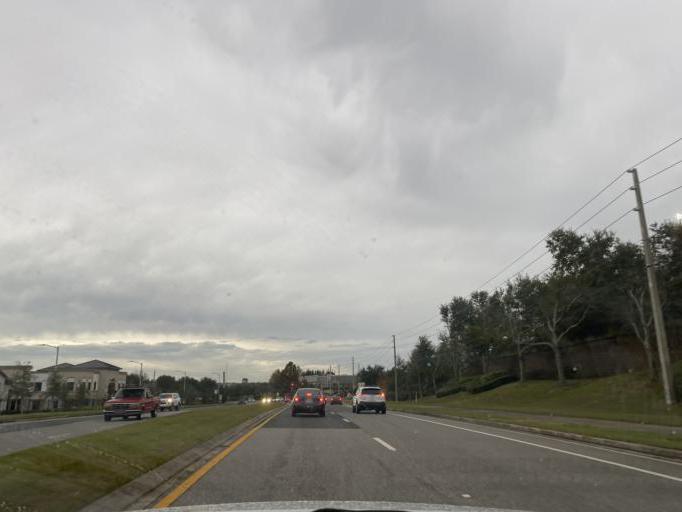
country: US
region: Florida
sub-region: Lake County
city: Minneola
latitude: 28.5294
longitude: -81.7285
